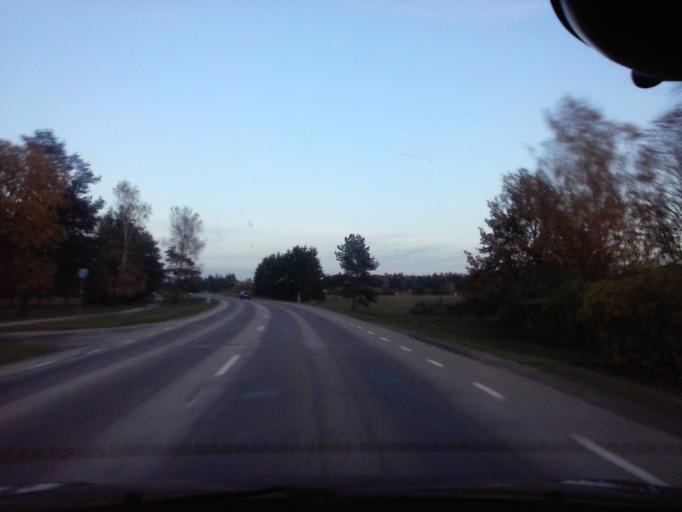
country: EE
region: Raplamaa
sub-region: Maerjamaa vald
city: Marjamaa
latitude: 58.9177
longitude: 24.4454
